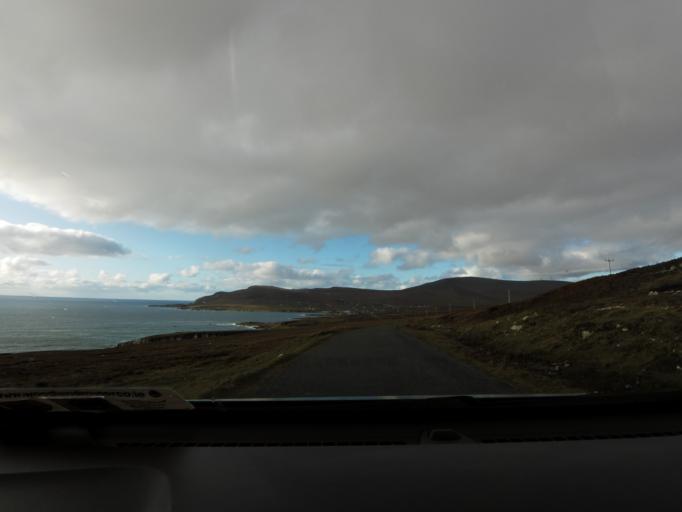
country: IE
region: Connaught
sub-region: Maigh Eo
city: Belmullet
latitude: 53.9088
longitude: -9.9998
